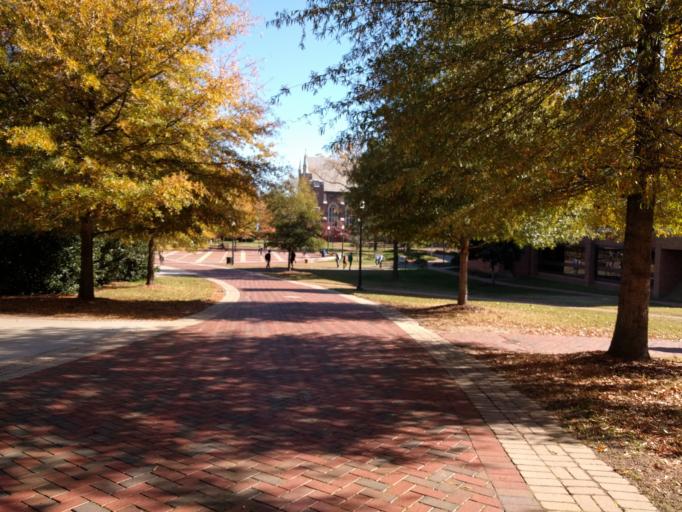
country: US
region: Virginia
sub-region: Henrico County
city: Tuckahoe
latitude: 37.5748
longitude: -77.5407
